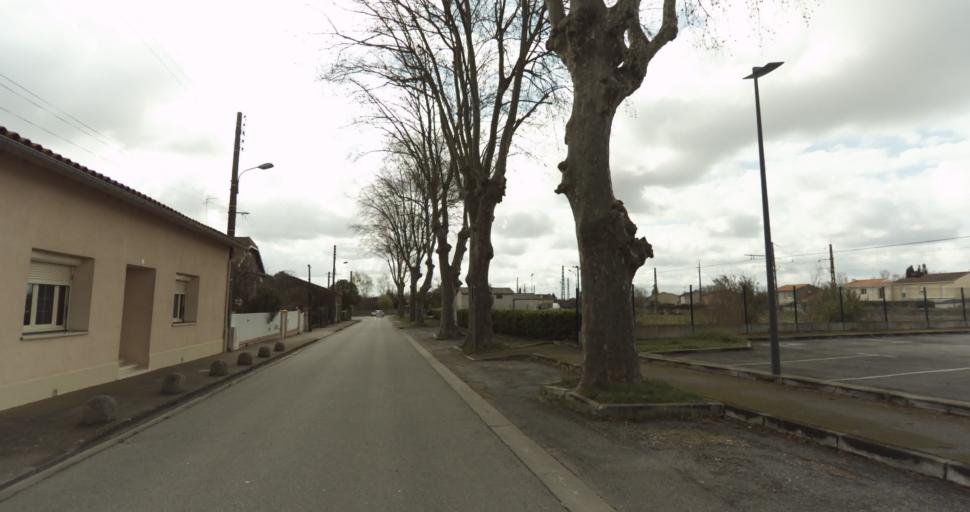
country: FR
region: Midi-Pyrenees
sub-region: Departement de la Haute-Garonne
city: Auterive
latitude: 43.3477
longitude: 1.4703
